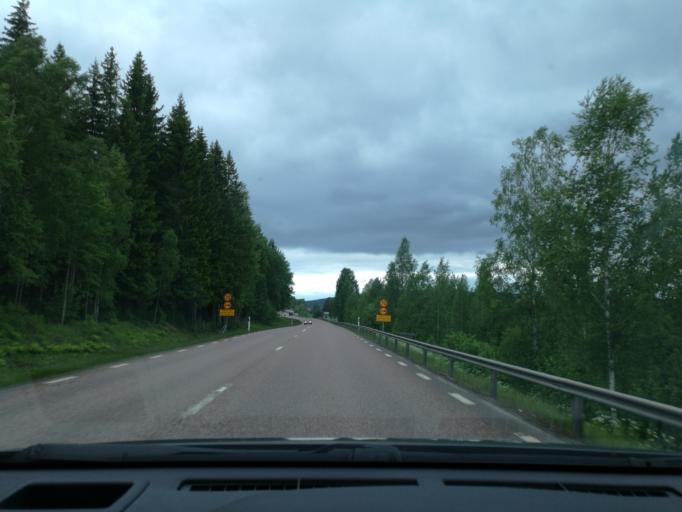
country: SE
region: Dalarna
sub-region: Smedjebackens Kommun
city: Smedjebacken
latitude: 60.1264
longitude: 15.4652
